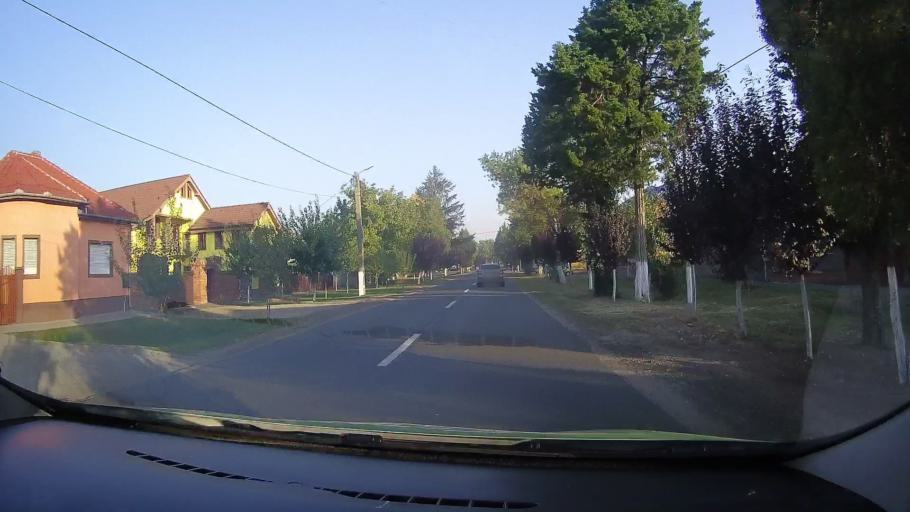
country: RO
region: Arad
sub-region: Comuna Curtici
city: Curtici
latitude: 46.3368
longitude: 21.3084
